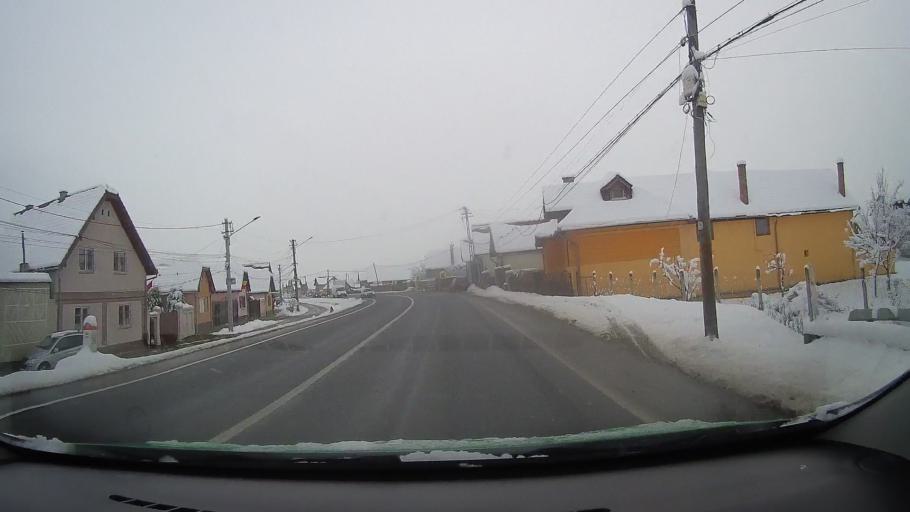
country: RO
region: Sibiu
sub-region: Comuna Cristian
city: Cristian
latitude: 45.7882
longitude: 24.0329
